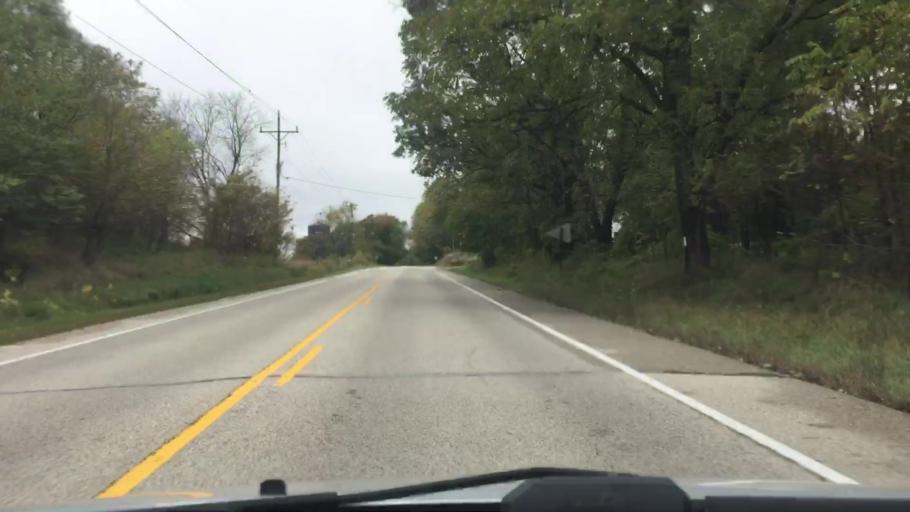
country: US
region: Wisconsin
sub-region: Waukesha County
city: Eagle
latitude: 42.8507
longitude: -88.5167
